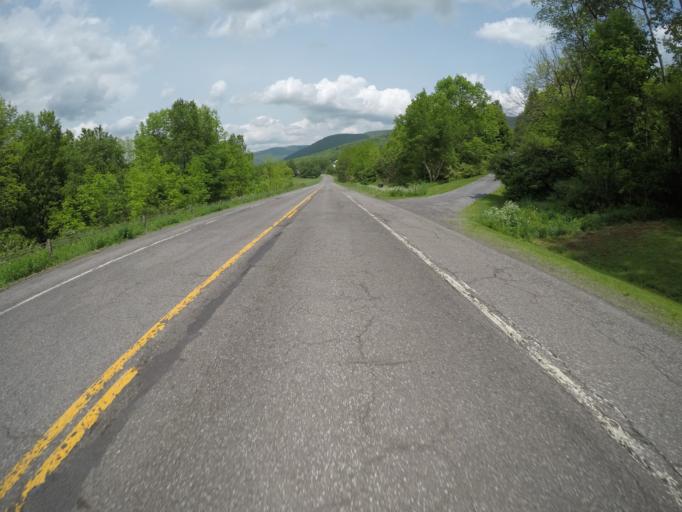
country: US
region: New York
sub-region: Delaware County
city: Stamford
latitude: 42.2649
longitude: -74.5841
